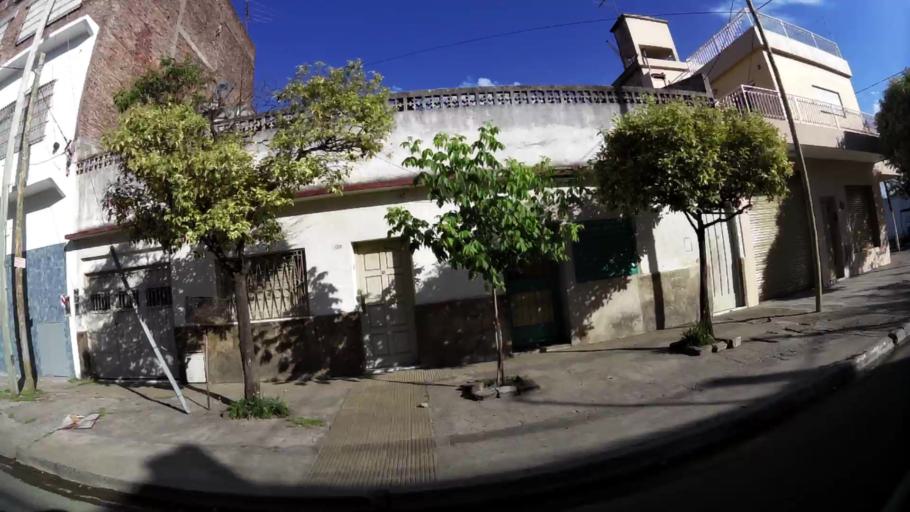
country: AR
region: Buenos Aires
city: Hurlingham
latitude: -34.5636
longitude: -58.6156
